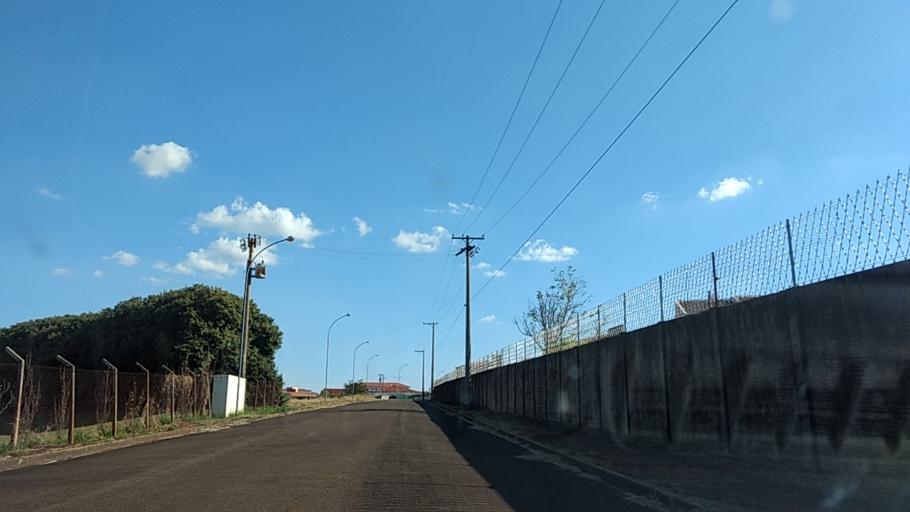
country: BR
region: Sao Paulo
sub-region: Botucatu
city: Botucatu
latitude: -22.8532
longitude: -48.4356
